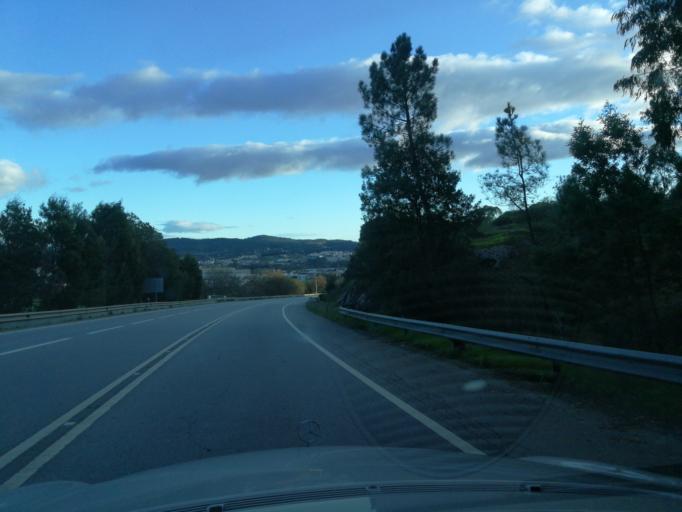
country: PT
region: Braga
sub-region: Barcelos
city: Vila Frescainha
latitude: 41.5390
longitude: -8.6402
